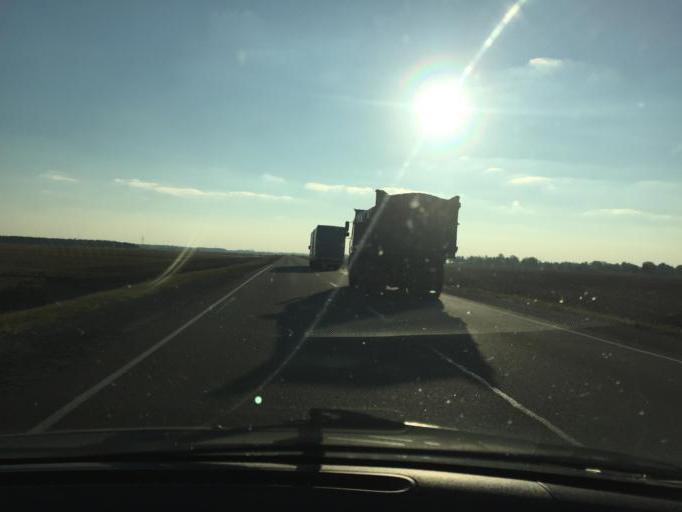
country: BY
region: Brest
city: Asnyezhytsy
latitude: 52.2915
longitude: 26.4189
